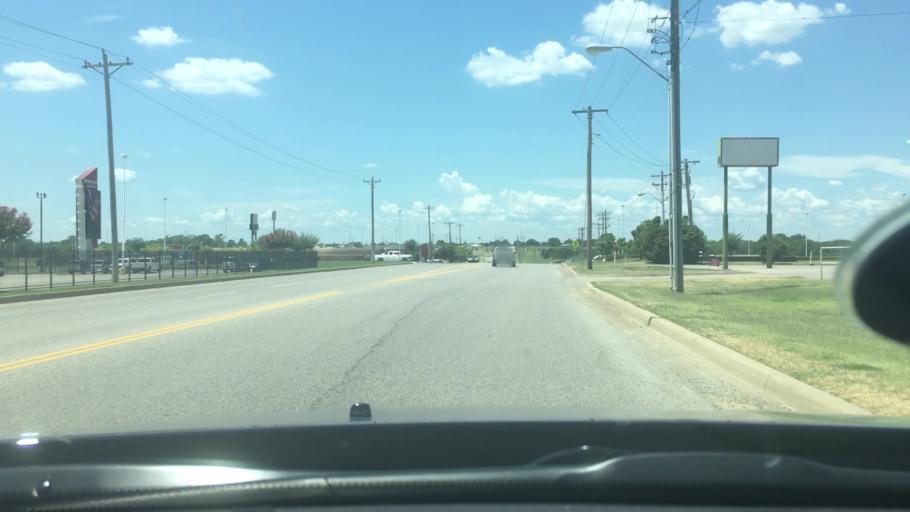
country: US
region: Oklahoma
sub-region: Bryan County
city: Calera
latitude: 33.9542
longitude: -96.4128
